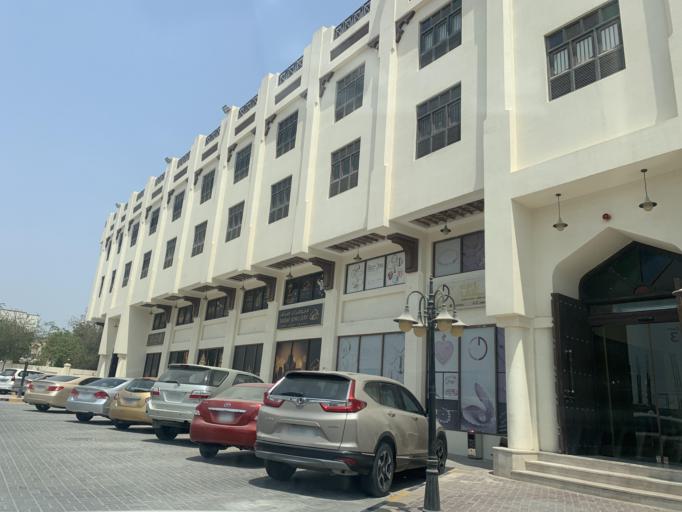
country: BH
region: Manama
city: Jidd Hafs
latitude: 26.2160
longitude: 50.4769
